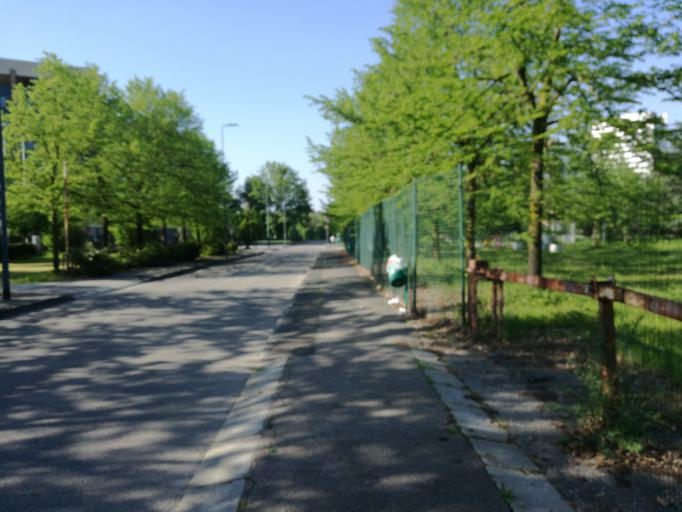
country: IT
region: Lombardy
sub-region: Citta metropolitana di Milano
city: Milano
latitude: 45.4336
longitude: 9.1908
